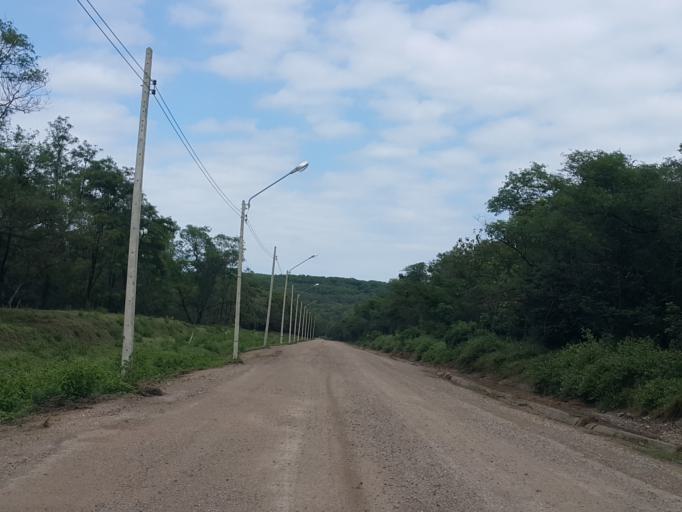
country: TH
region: Lampang
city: Mae Mo
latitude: 18.3188
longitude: 99.7484
